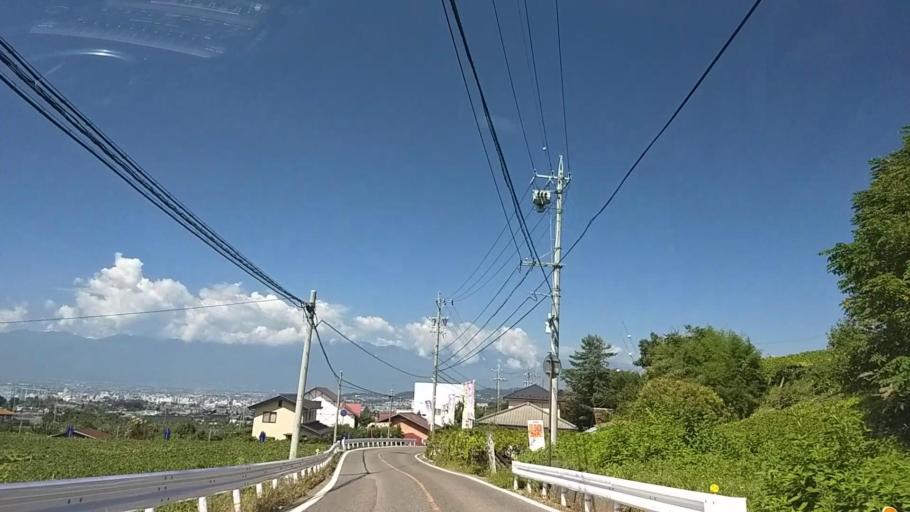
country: JP
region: Nagano
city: Matsumoto
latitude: 36.2313
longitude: 138.0198
